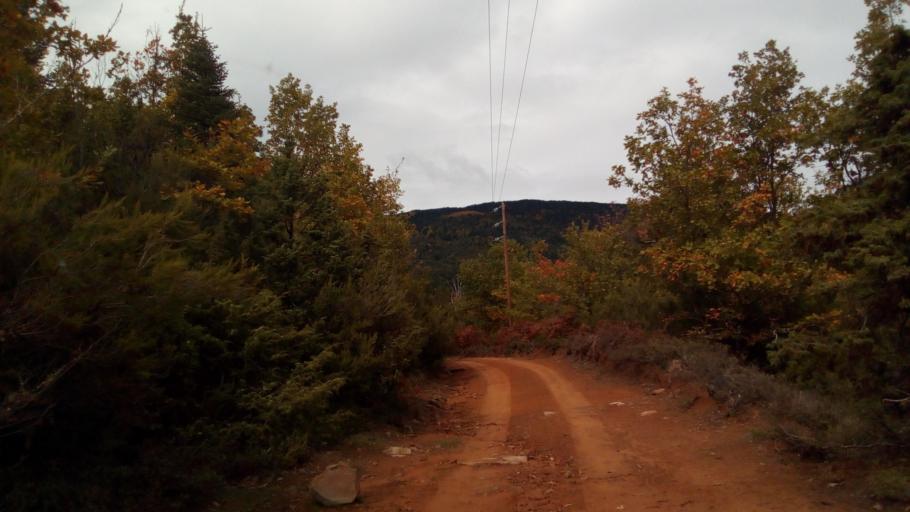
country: GR
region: West Greece
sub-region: Nomos Aitolias kai Akarnanias
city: Nafpaktos
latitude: 38.5576
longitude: 21.9653
